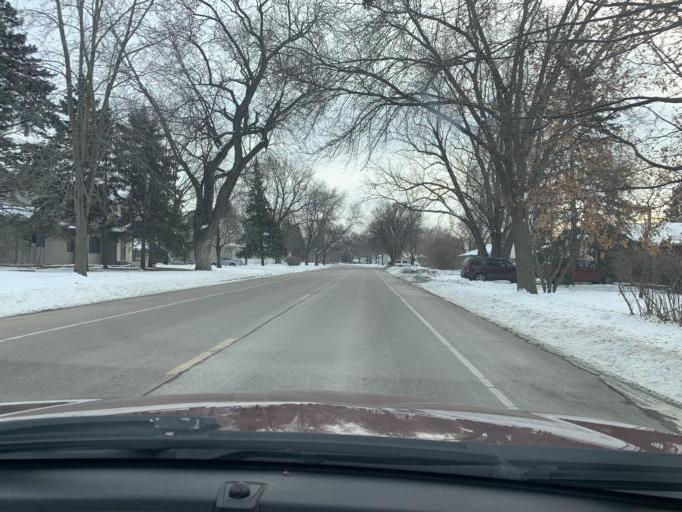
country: US
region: Minnesota
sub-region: Washington County
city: Saint Paul Park
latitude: 44.8418
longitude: -92.9915
